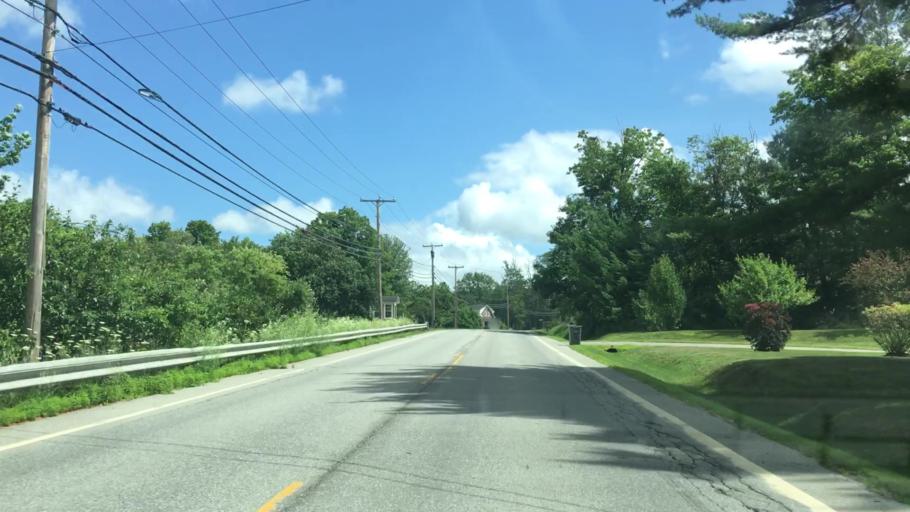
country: US
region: Maine
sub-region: Penobscot County
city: Carmel
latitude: 44.8014
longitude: -69.0380
